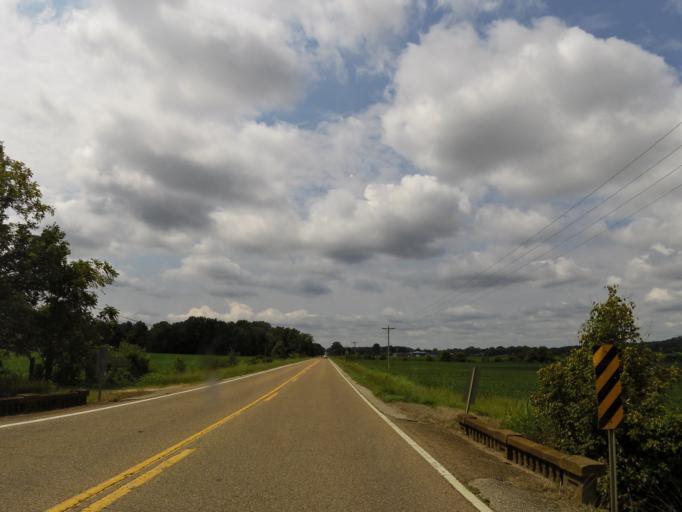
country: US
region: Tennessee
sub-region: Decatur County
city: Decaturville
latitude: 35.5184
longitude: -88.2803
